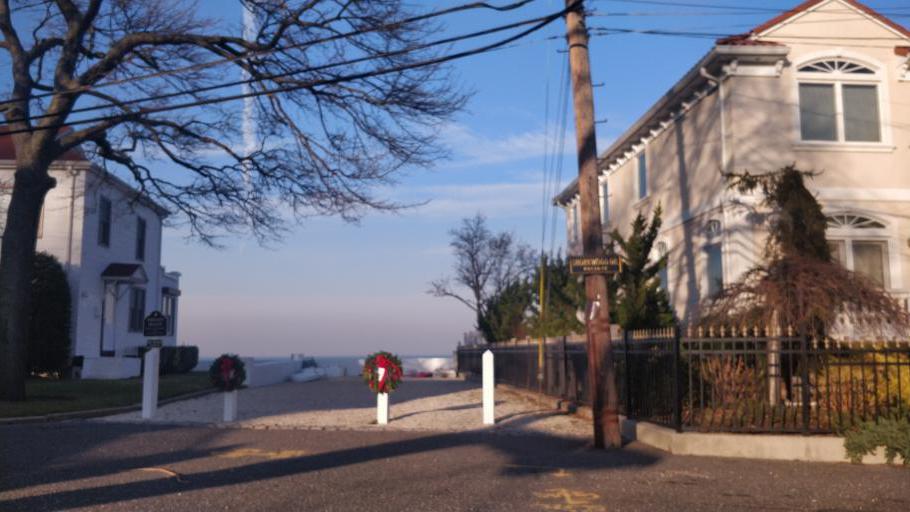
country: US
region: New York
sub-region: Nassau County
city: Bayville
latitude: 40.9108
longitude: -73.5573
